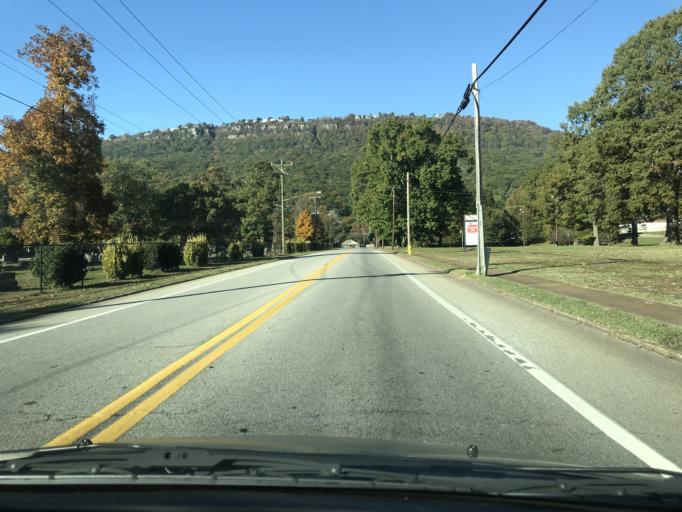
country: US
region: Tennessee
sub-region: Hamilton County
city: Lookout Mountain
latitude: 35.0082
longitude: -85.3236
